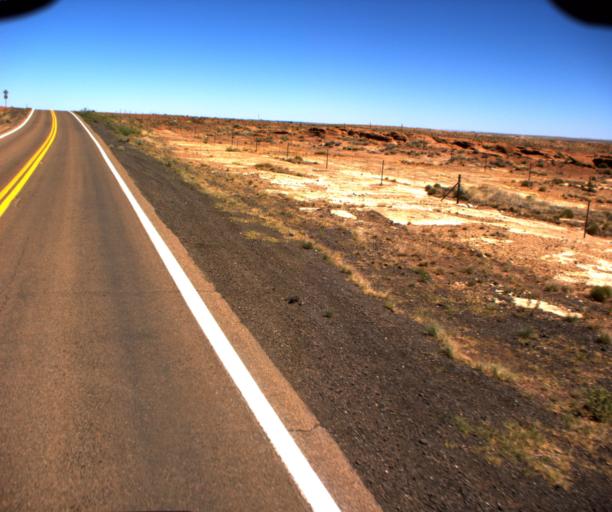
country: US
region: Arizona
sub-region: Navajo County
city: Winslow
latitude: 34.9711
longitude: -110.6480
